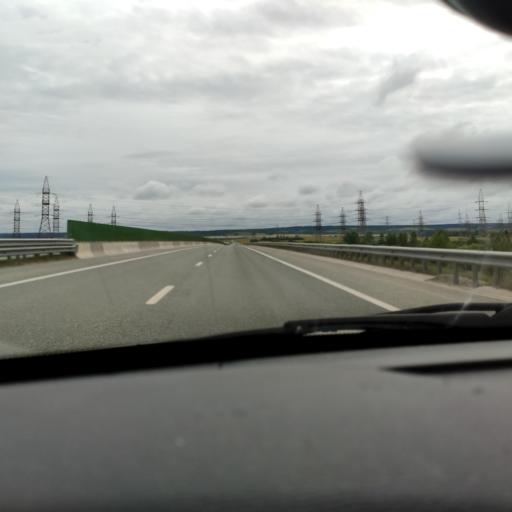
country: RU
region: Perm
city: Froly
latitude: 57.9301
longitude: 56.3000
